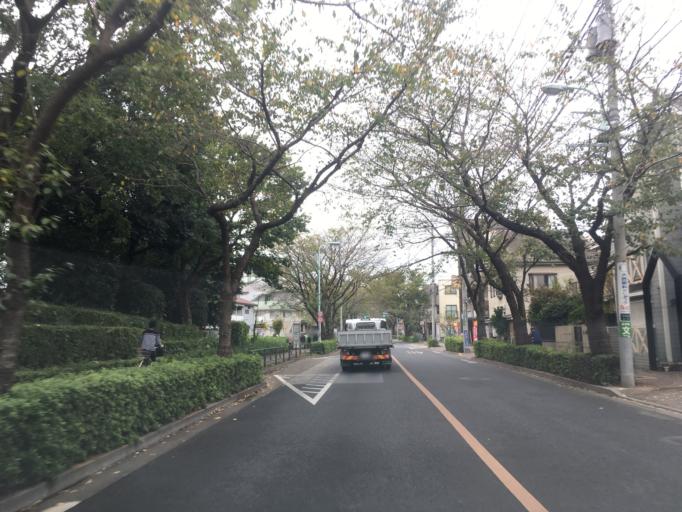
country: JP
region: Tokyo
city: Chofugaoka
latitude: 35.6333
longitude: 139.5697
